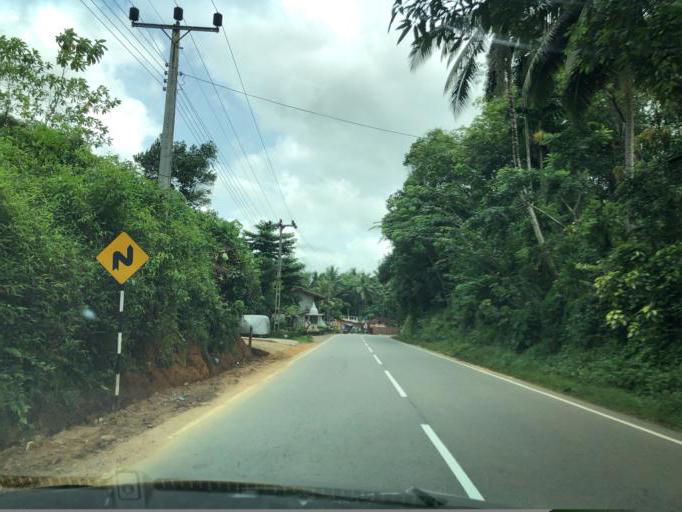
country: LK
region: Western
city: Horana South
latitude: 6.6903
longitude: 80.1386
